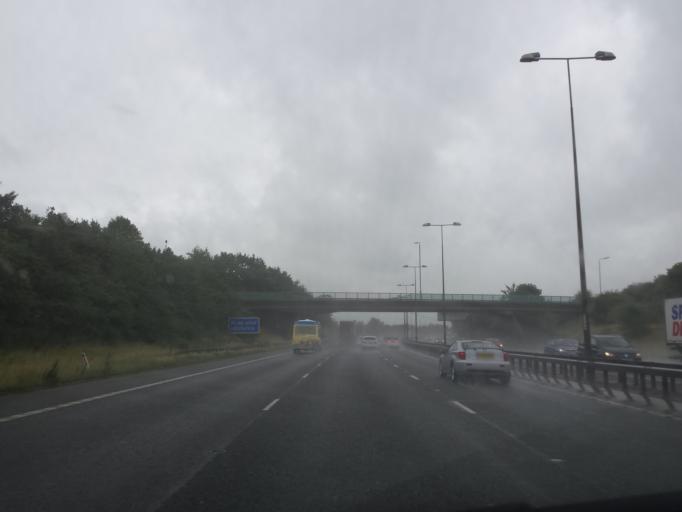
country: GB
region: England
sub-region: Derbyshire
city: Long Eaton
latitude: 52.8998
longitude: -1.2984
